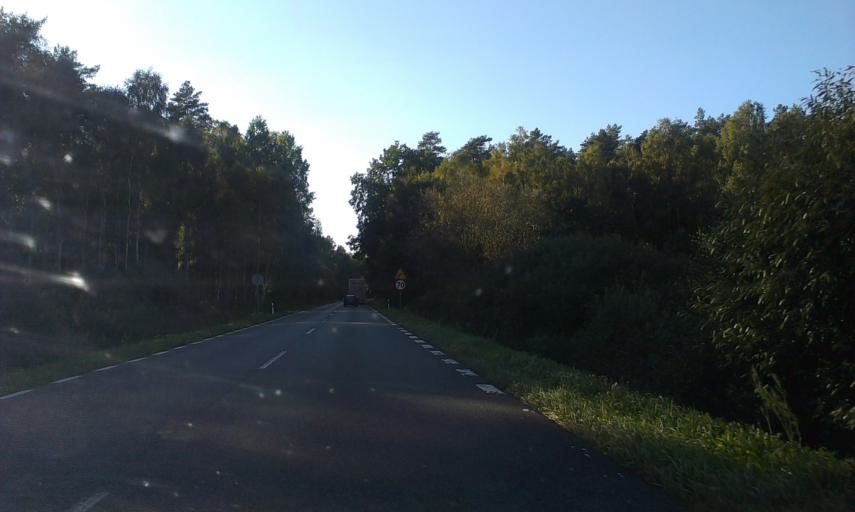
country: PL
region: Kujawsko-Pomorskie
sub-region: Powiat swiecki
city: Swiekatowo
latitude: 53.4895
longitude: 18.1006
